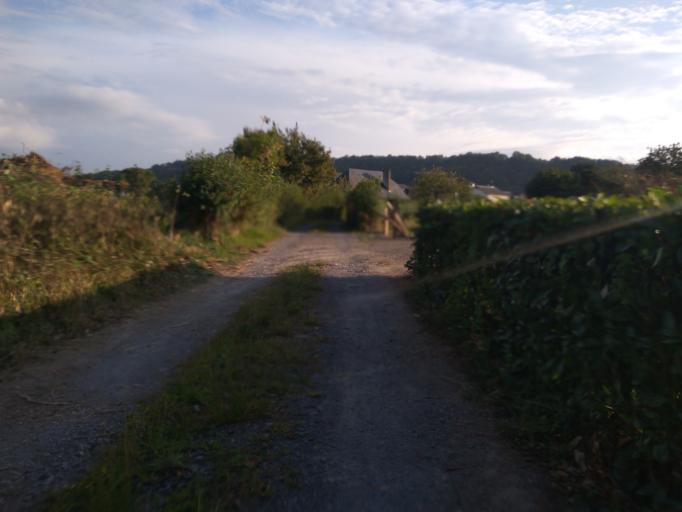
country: FR
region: Aquitaine
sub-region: Departement des Pyrenees-Atlantiques
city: Bizanos
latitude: 43.2794
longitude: -0.3526
